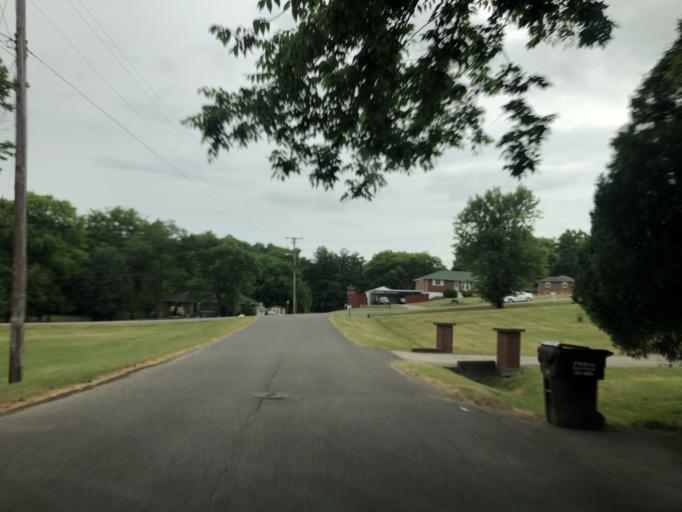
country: US
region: Tennessee
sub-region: Davidson County
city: Goodlettsville
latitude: 36.2665
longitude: -86.7731
